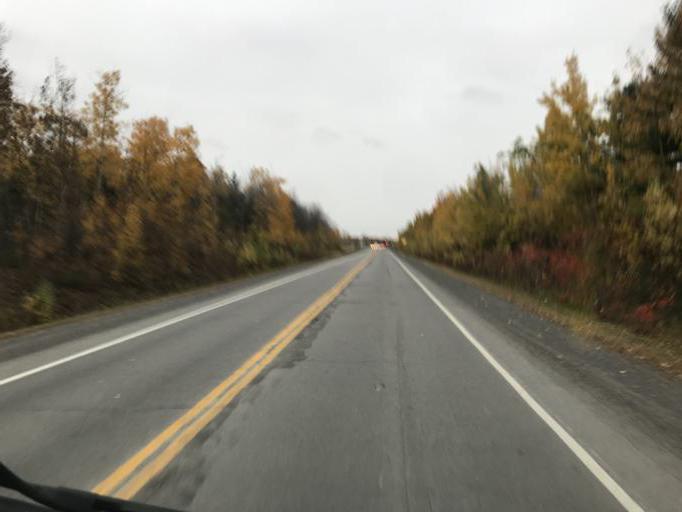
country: CA
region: Quebec
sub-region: Lanaudiere
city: Lorraine
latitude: 45.6844
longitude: -73.7754
